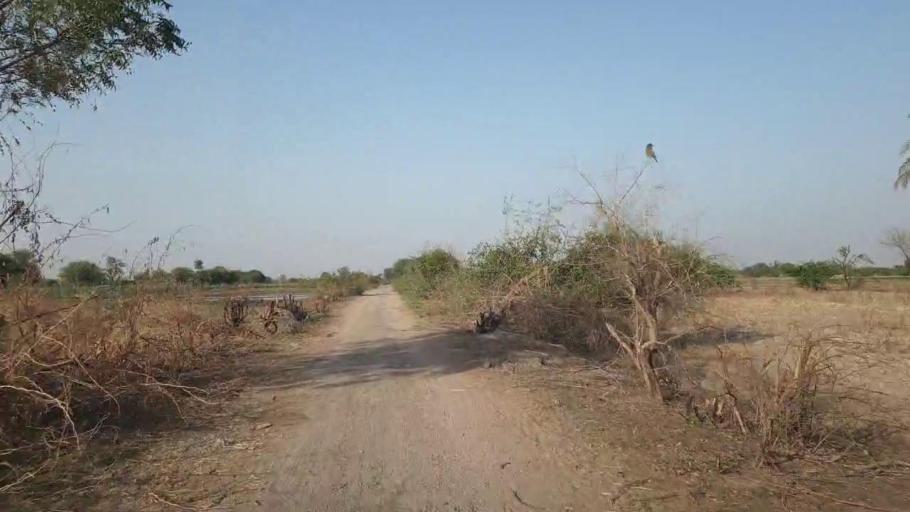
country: PK
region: Sindh
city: Dhoro Naro
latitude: 25.4931
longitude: 69.5755
